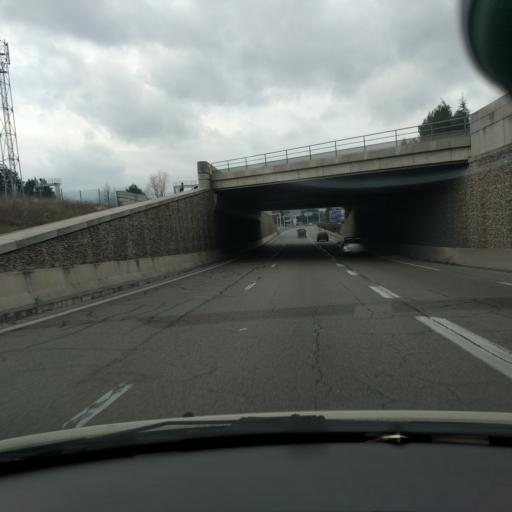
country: FR
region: Provence-Alpes-Cote d'Azur
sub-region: Departement des Bouches-du-Rhone
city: Gardanne
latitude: 43.4633
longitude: 5.4658
